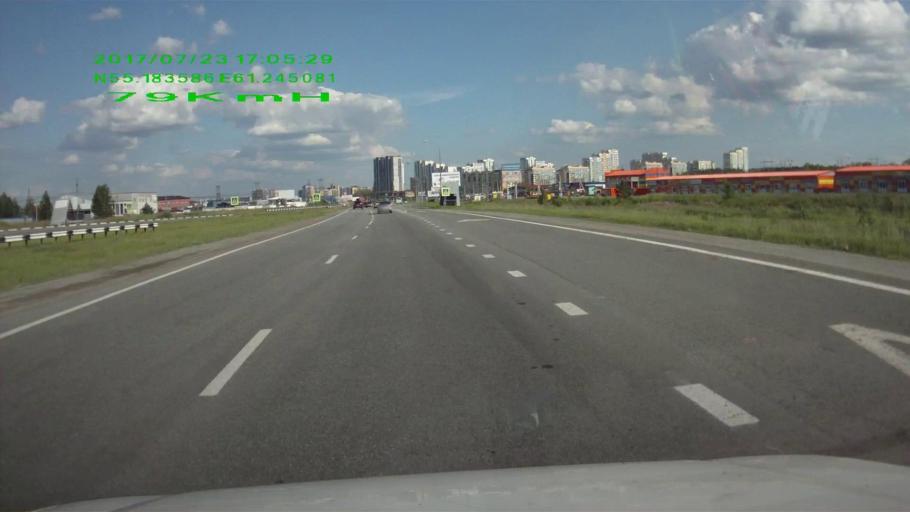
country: RU
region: Chelyabinsk
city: Roshchino
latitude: 55.1826
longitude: 61.2464
